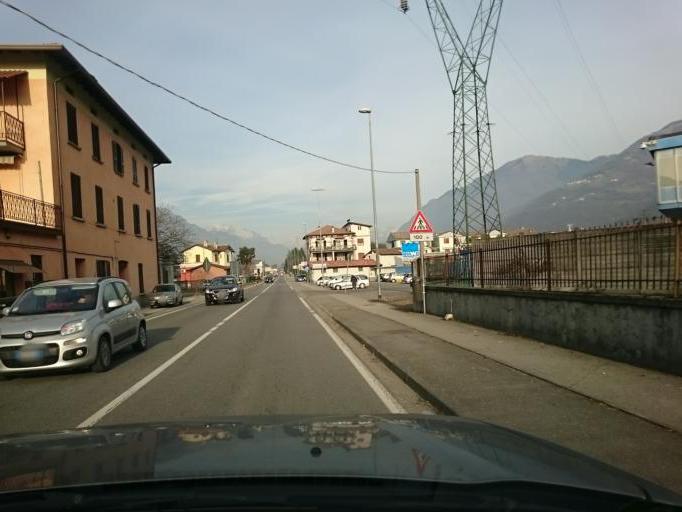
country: IT
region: Lombardy
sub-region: Provincia di Brescia
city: Pian Camuno
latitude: 45.8391
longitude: 10.1381
